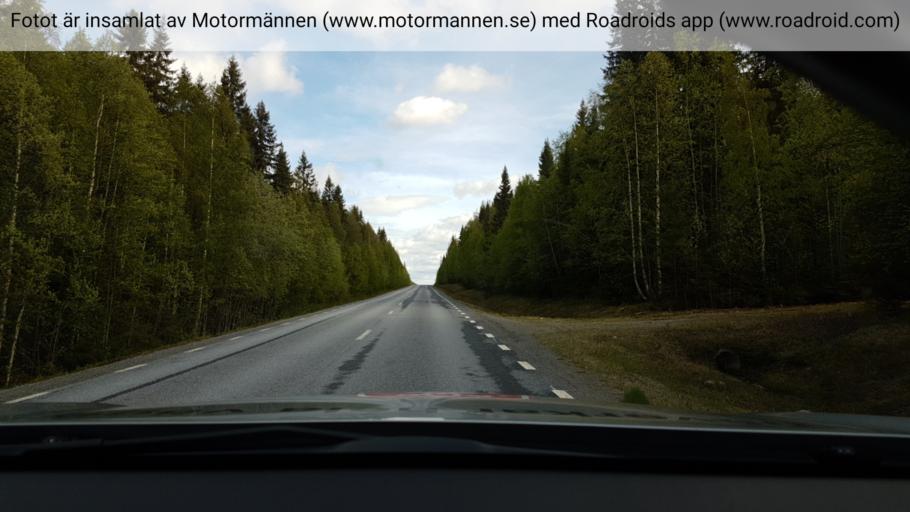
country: SE
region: Vaesterbotten
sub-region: Lycksele Kommun
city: Lycksele
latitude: 64.0517
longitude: 18.5576
